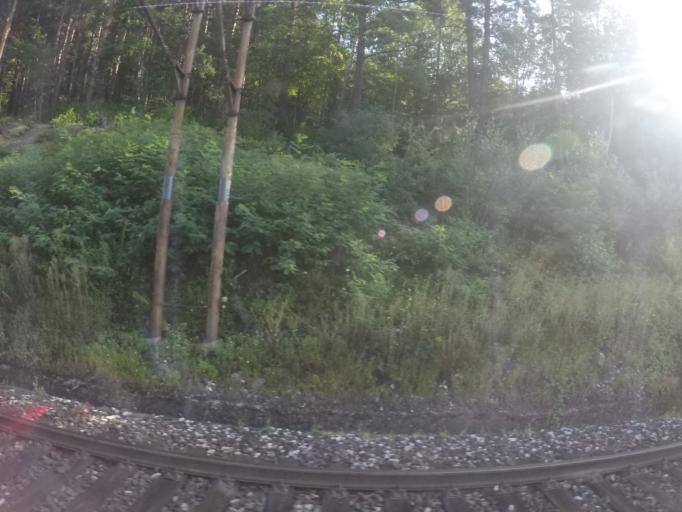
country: SK
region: Kosicky
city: Gelnica
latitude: 48.8918
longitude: 21.0347
